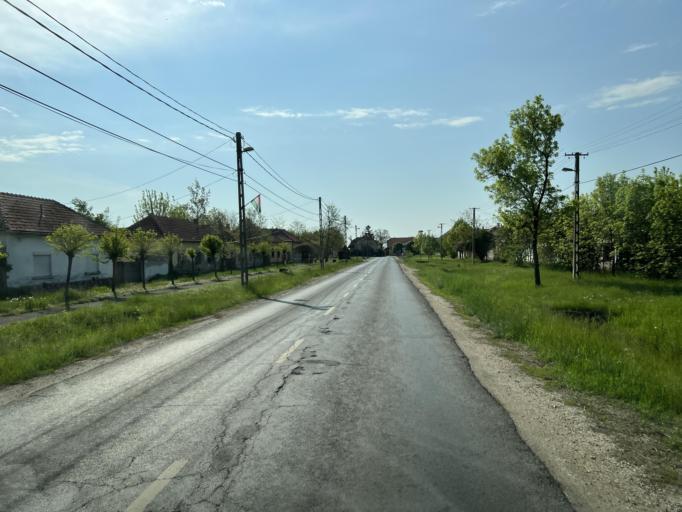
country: HU
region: Pest
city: Jaszkarajeno
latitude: 47.0495
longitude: 20.0723
